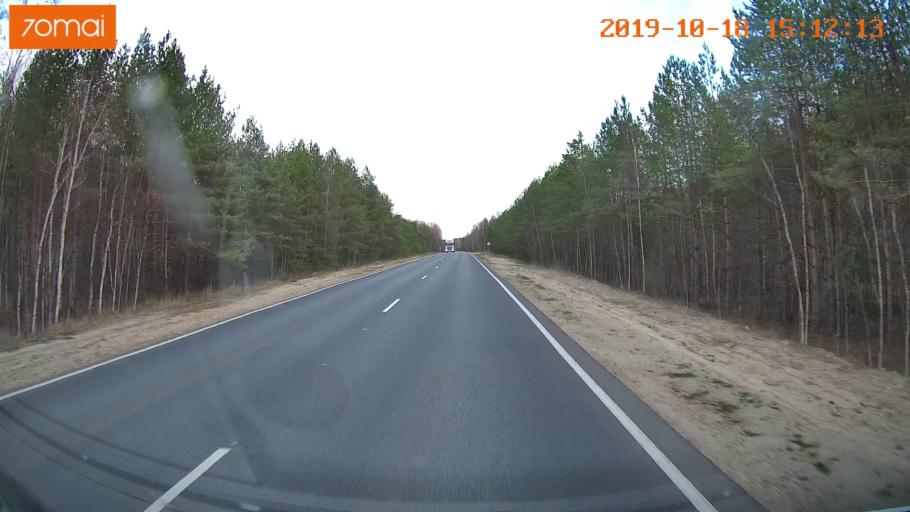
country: RU
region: Vladimir
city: Gus'-Khrustal'nyy
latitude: 55.5749
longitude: 40.6918
